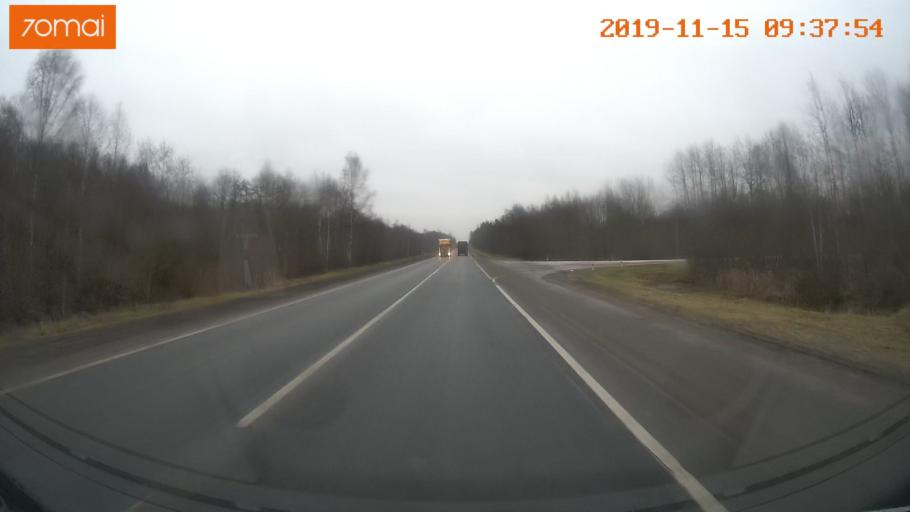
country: RU
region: Vologda
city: Sheksna
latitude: 59.2367
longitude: 38.4454
